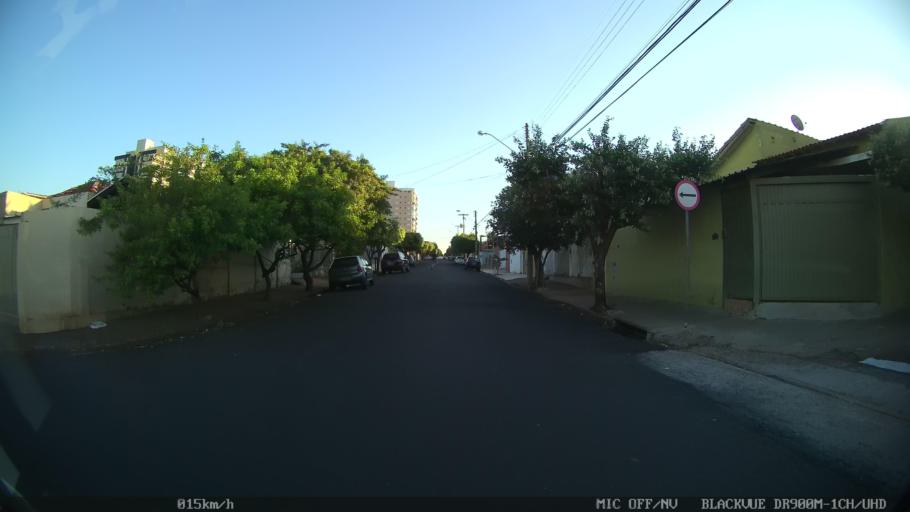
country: BR
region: Sao Paulo
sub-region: Sao Jose Do Rio Preto
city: Sao Jose do Rio Preto
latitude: -20.8005
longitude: -49.3813
